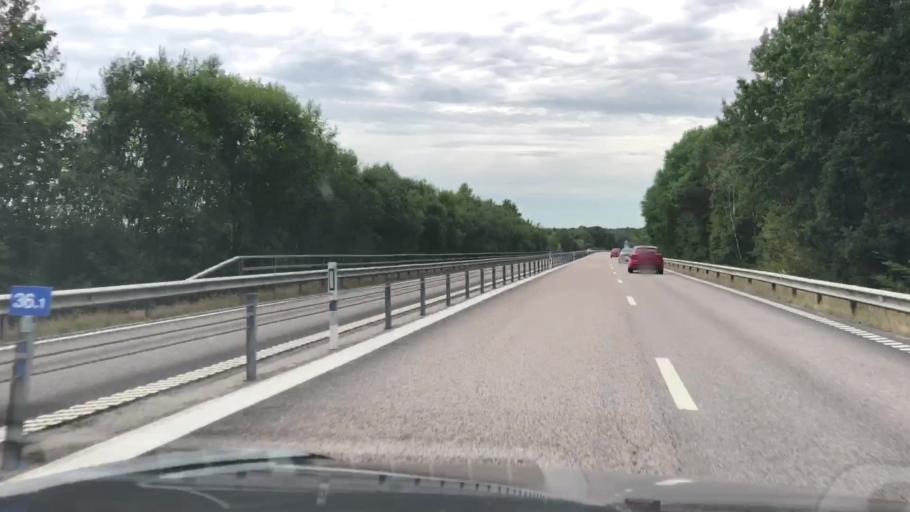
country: SE
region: Blekinge
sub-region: Karlshamns Kommun
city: Karlshamn
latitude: 56.1949
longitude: 14.9682
